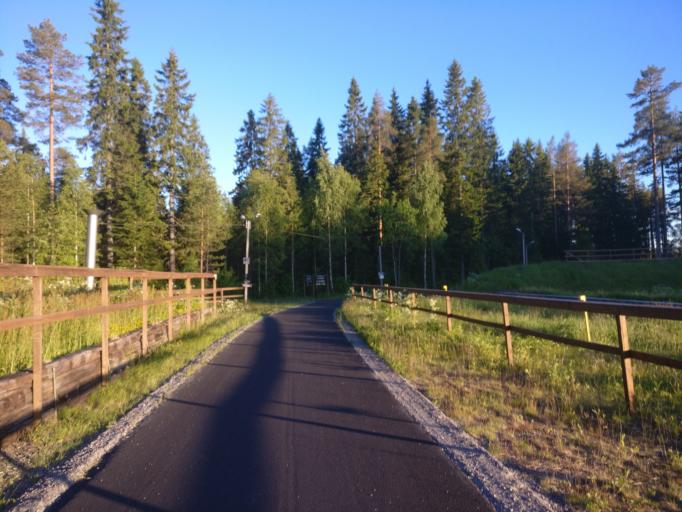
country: SE
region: Vaesternorrland
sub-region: Timra Kommun
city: Timra
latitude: 62.4610
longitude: 17.2941
